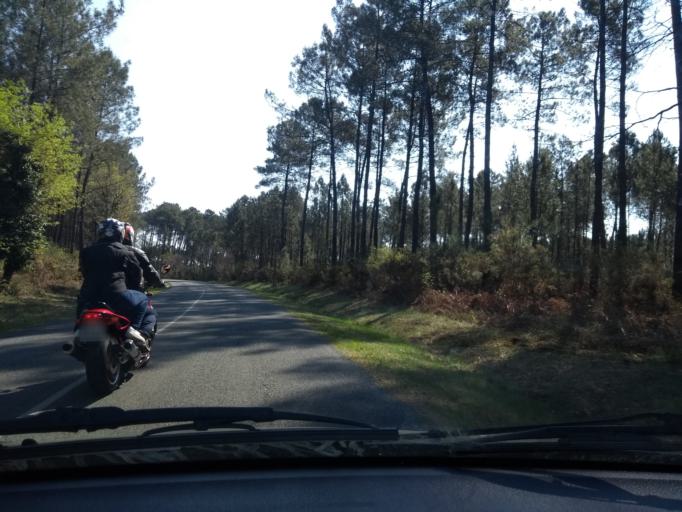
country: FR
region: Aquitaine
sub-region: Departement de la Gironde
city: Belin-Beliet
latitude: 44.5201
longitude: -0.7486
